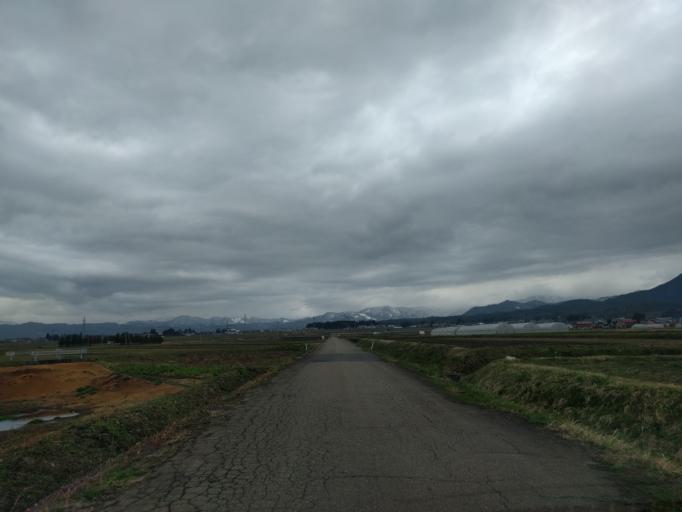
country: JP
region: Fukushima
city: Kitakata
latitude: 37.6452
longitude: 139.9181
